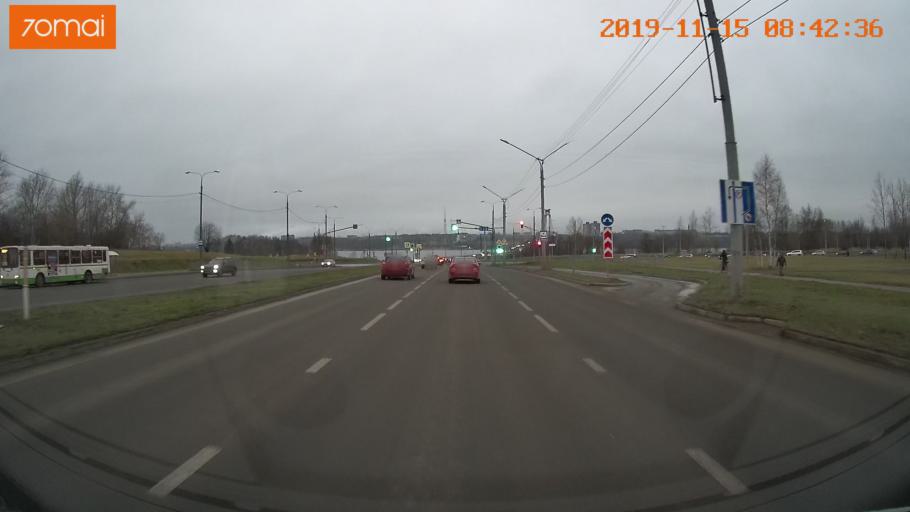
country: RU
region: Vologda
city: Cherepovets
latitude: 59.1041
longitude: 37.9071
